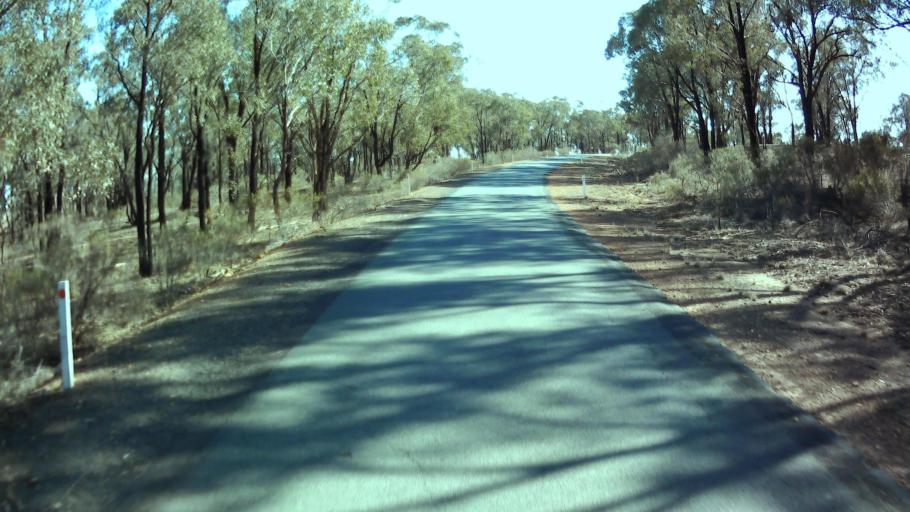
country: AU
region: New South Wales
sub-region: Weddin
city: Grenfell
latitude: -33.7843
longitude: 147.9589
